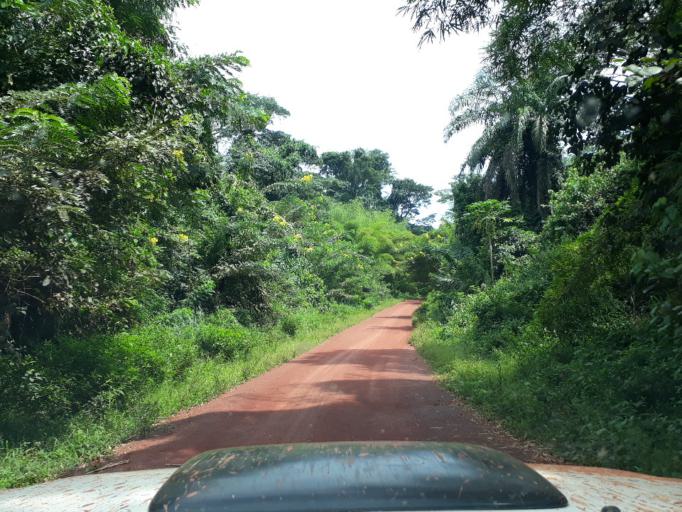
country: CD
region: Eastern Province
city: Buta
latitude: 2.3821
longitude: 24.9206
